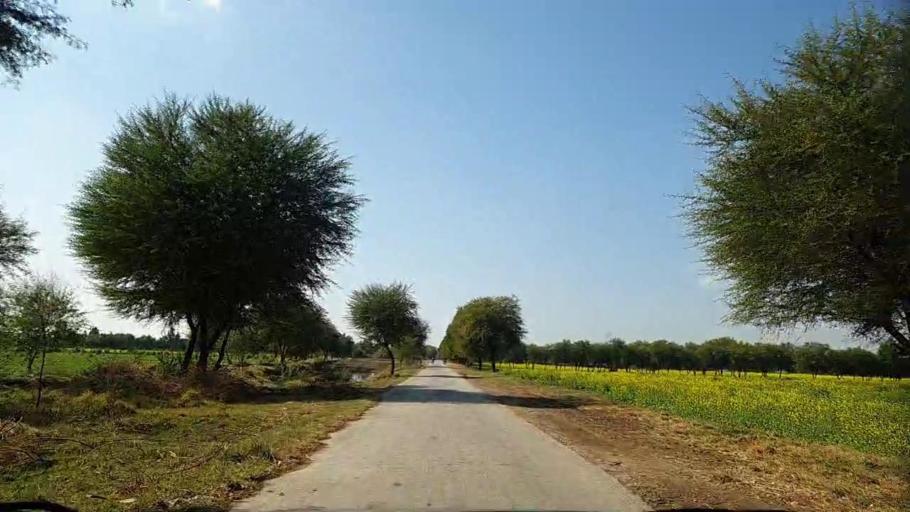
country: PK
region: Sindh
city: Pithoro
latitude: 25.6661
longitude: 69.4562
